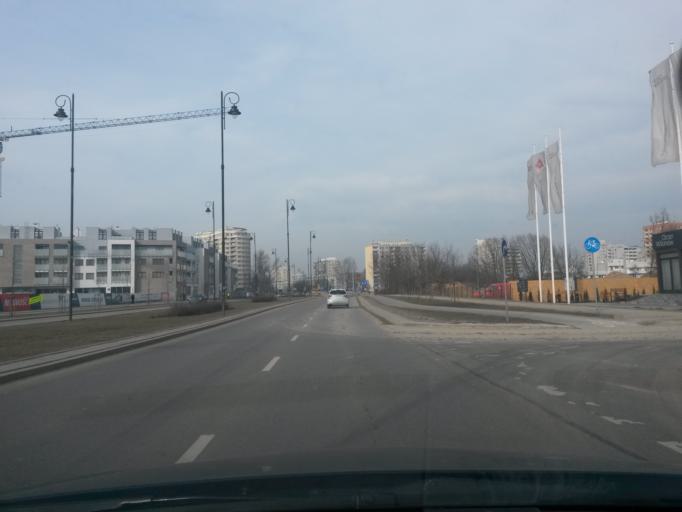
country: PL
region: Masovian Voivodeship
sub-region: Warszawa
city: Wilanow
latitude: 52.1672
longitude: 21.0691
